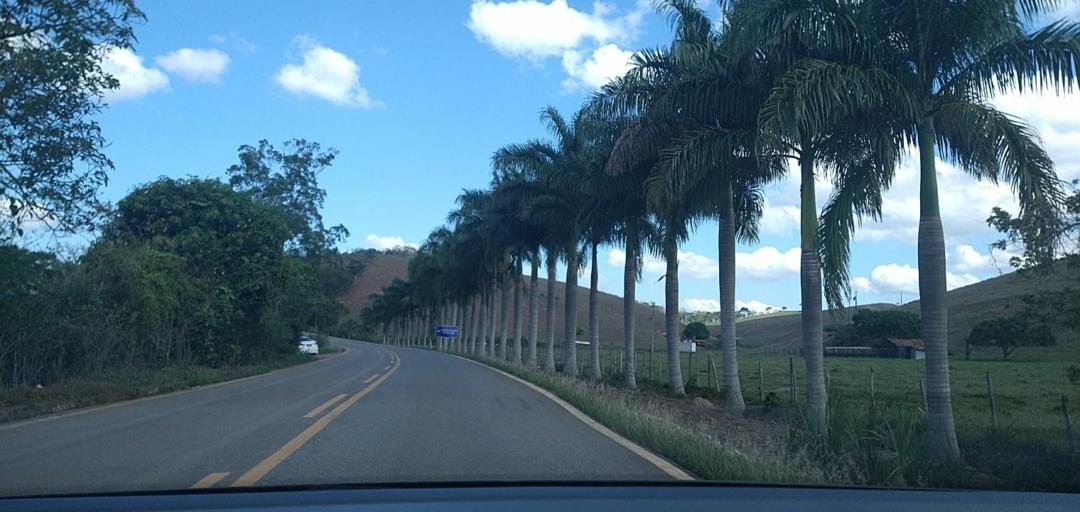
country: BR
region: Minas Gerais
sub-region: Alvinopolis
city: Alvinopolis
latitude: -20.0259
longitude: -43.0604
